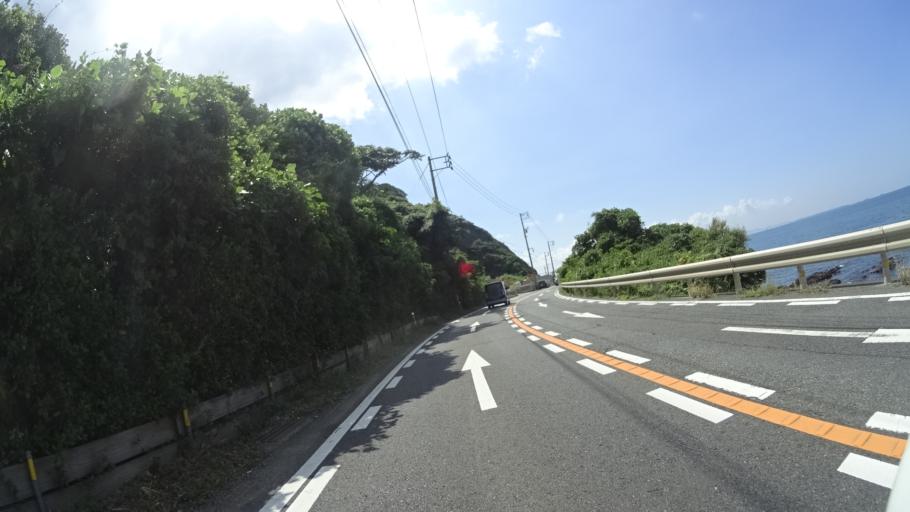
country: JP
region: Yamaguchi
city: Shimonoseki
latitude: 34.0583
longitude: 130.9124
